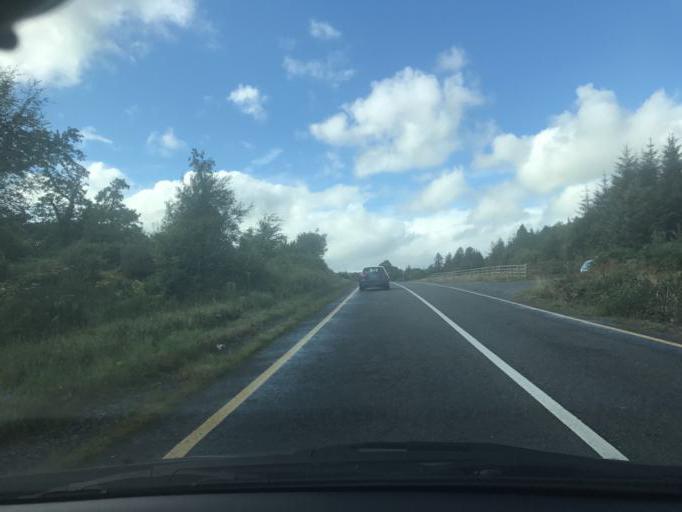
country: IE
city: Ballisodare
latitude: 54.2105
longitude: -8.4671
